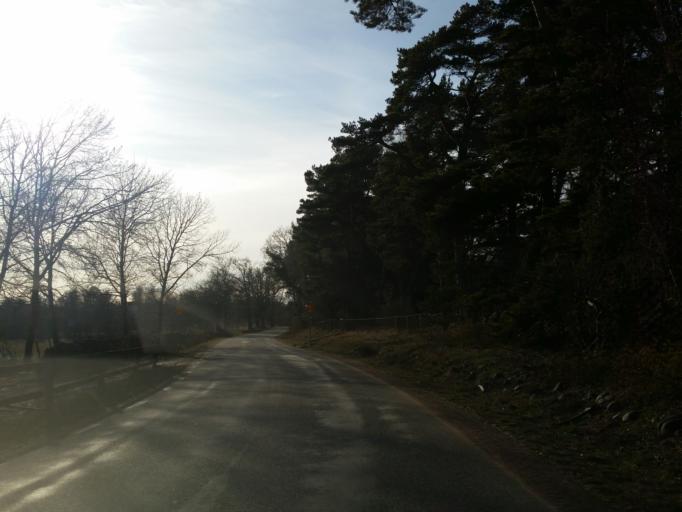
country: SE
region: Kalmar
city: Faerjestaden
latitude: 56.7742
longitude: 16.4670
